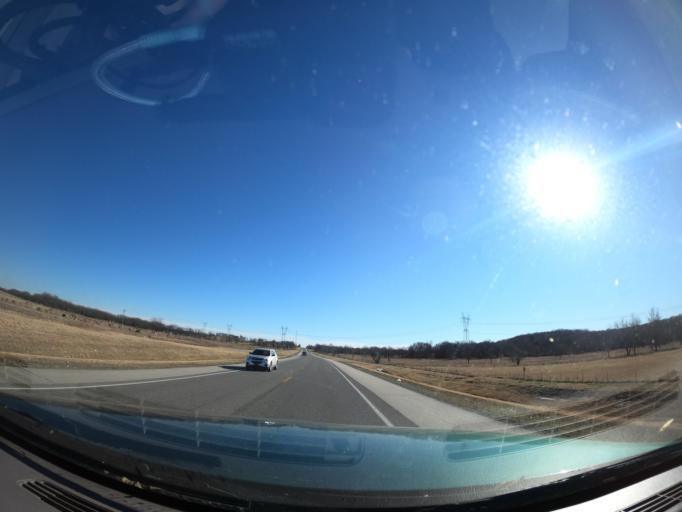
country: US
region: Oklahoma
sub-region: Muskogee County
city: Haskell
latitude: 35.7849
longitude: -95.6645
